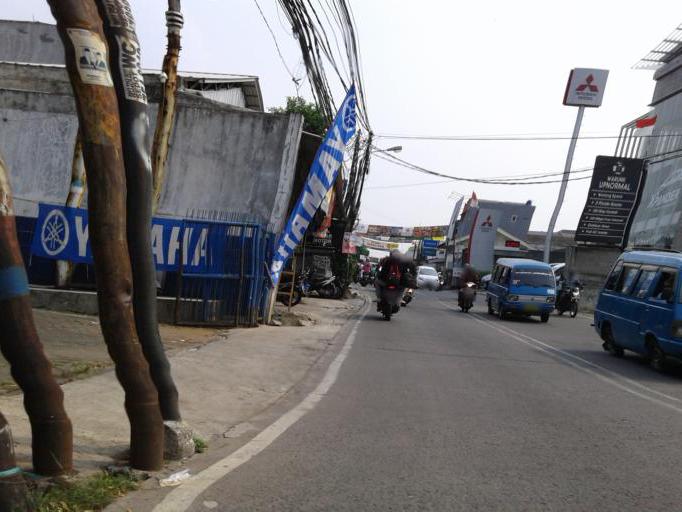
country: ID
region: West Java
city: Pamulang
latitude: -6.3296
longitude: 106.7843
